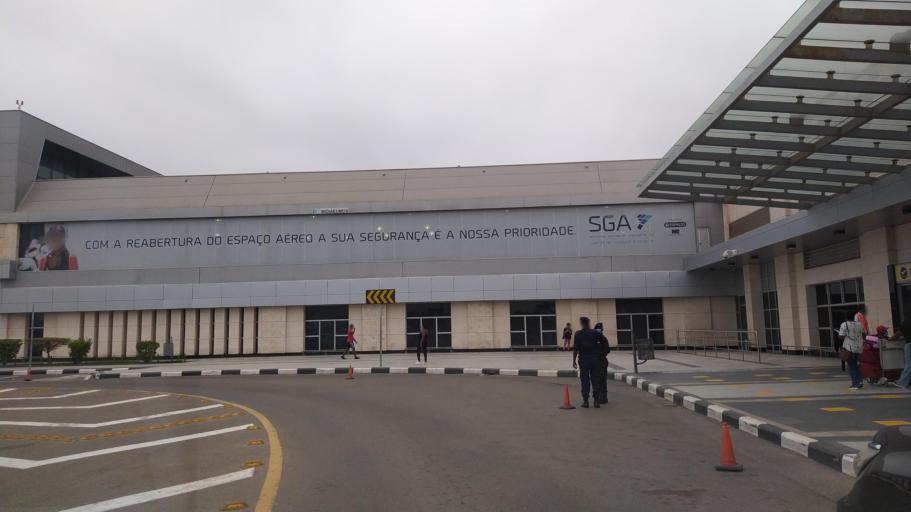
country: AO
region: Luanda
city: Luanda
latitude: -8.8476
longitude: 13.2353
